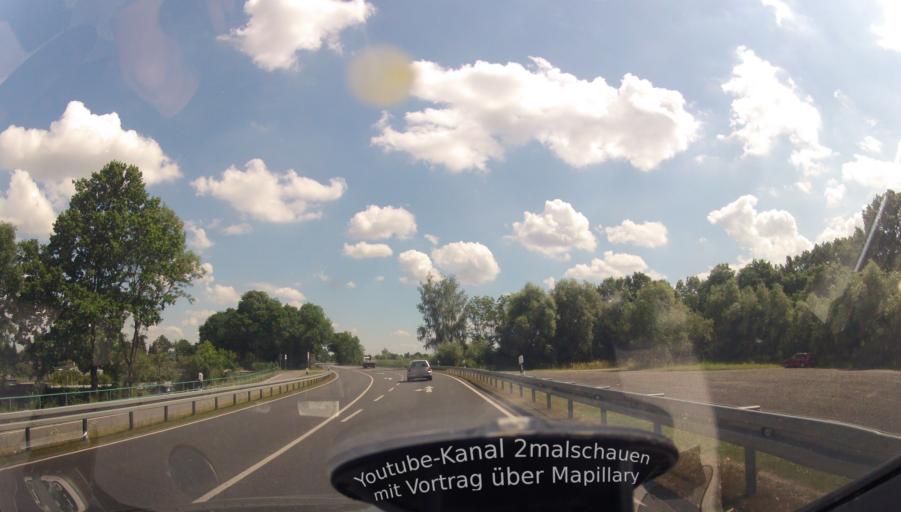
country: DE
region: Saxony
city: Torgau
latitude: 51.5419
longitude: 12.9990
